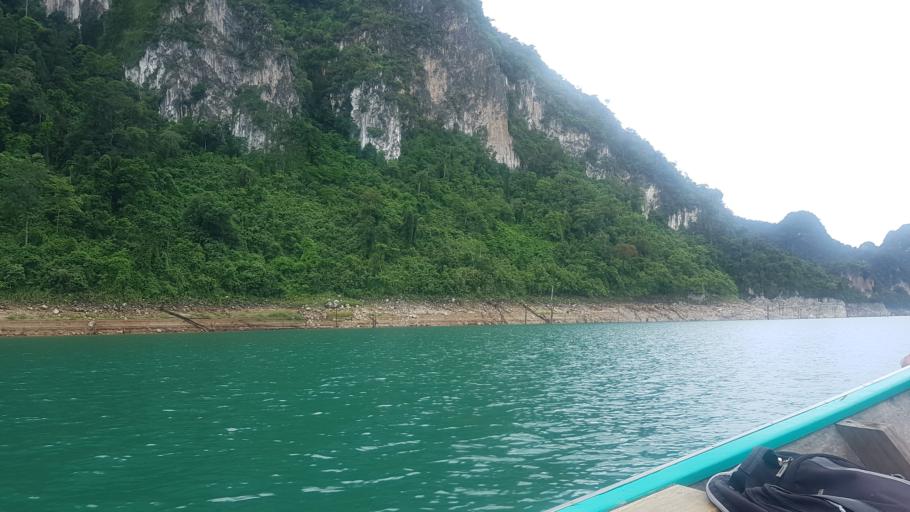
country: TH
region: Surat Thani
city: Phanom
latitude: 9.0306
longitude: 98.7186
